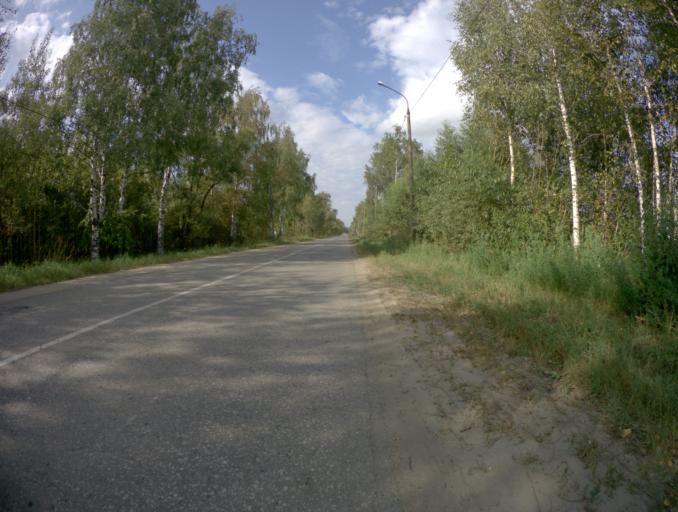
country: RU
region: Vladimir
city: Golovino
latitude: 55.9547
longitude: 40.4320
